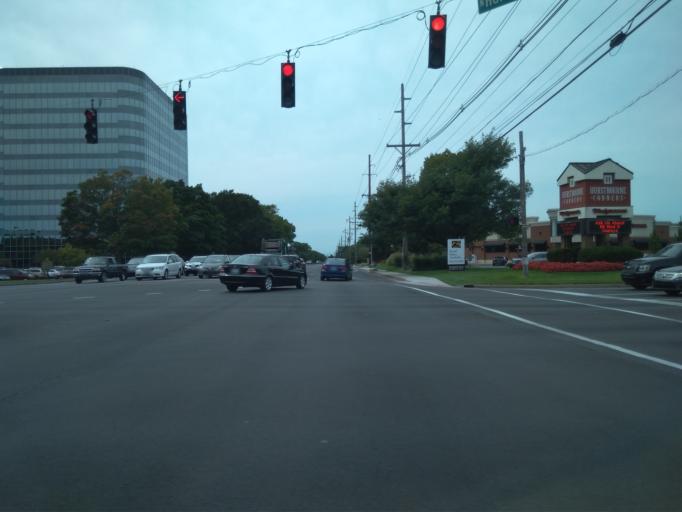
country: US
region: Kentucky
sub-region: Jefferson County
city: Hurstbourne
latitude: 38.2464
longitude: -85.5768
